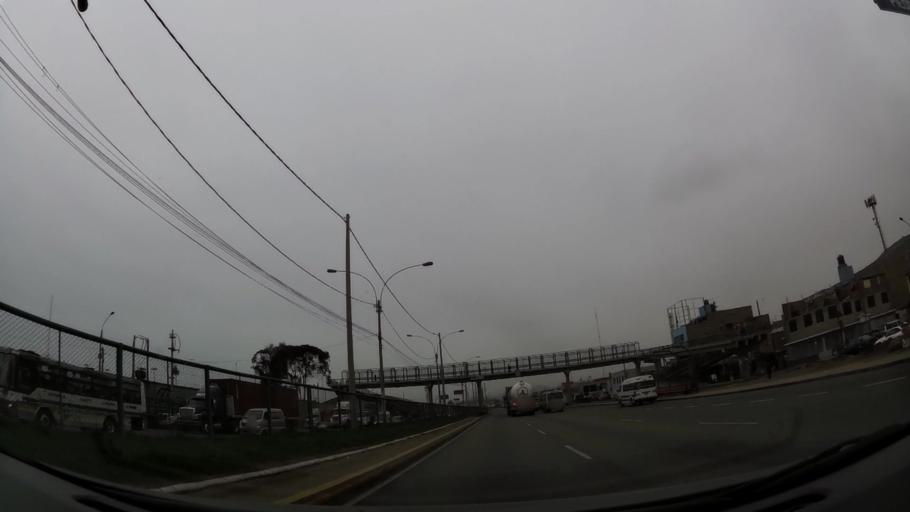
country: PE
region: Callao
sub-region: Callao
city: Callao
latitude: -11.9941
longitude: -77.1258
